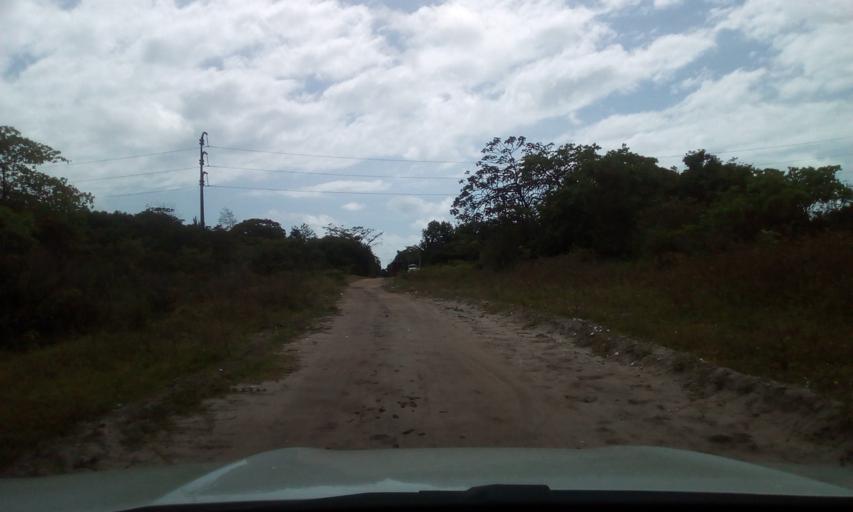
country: BR
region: Paraiba
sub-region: Joao Pessoa
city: Joao Pessoa
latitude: -7.1435
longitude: -34.8226
